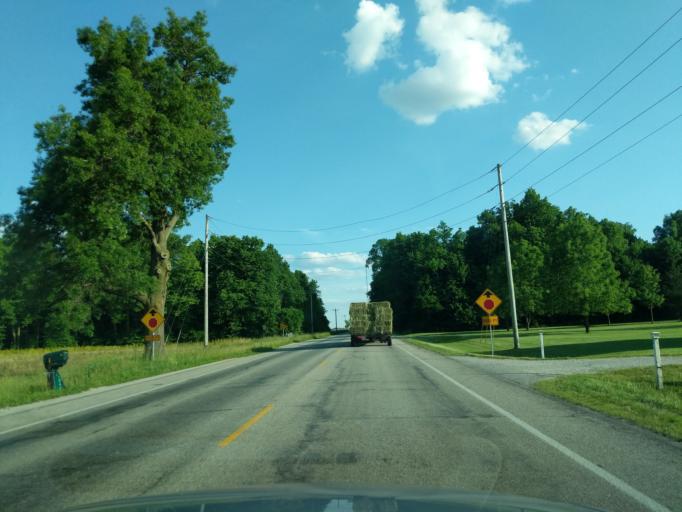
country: US
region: Indiana
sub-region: Huntington County
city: Roanoke
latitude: 41.0092
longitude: -85.4707
